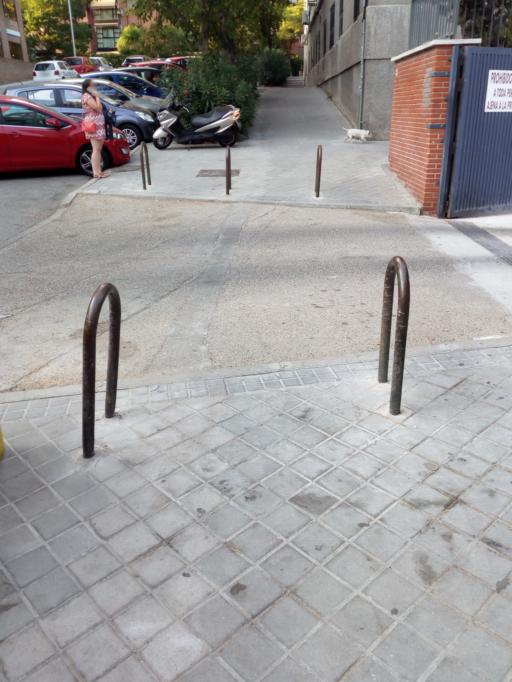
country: ES
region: Madrid
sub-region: Provincia de Madrid
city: Puente de Vallecas
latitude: 40.4078
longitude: -3.6667
